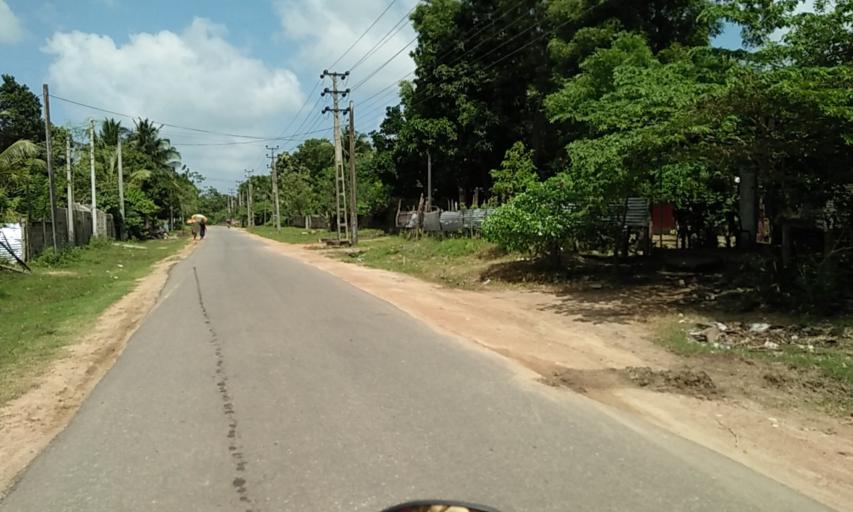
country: LK
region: Eastern Province
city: Ampara
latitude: 7.3340
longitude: 81.7428
